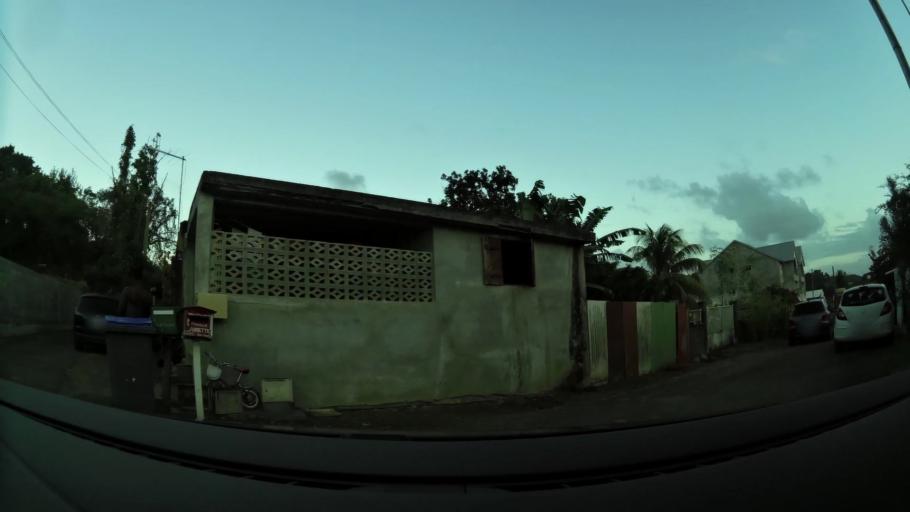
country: GP
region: Guadeloupe
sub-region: Guadeloupe
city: Les Abymes
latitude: 16.2820
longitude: -61.5009
